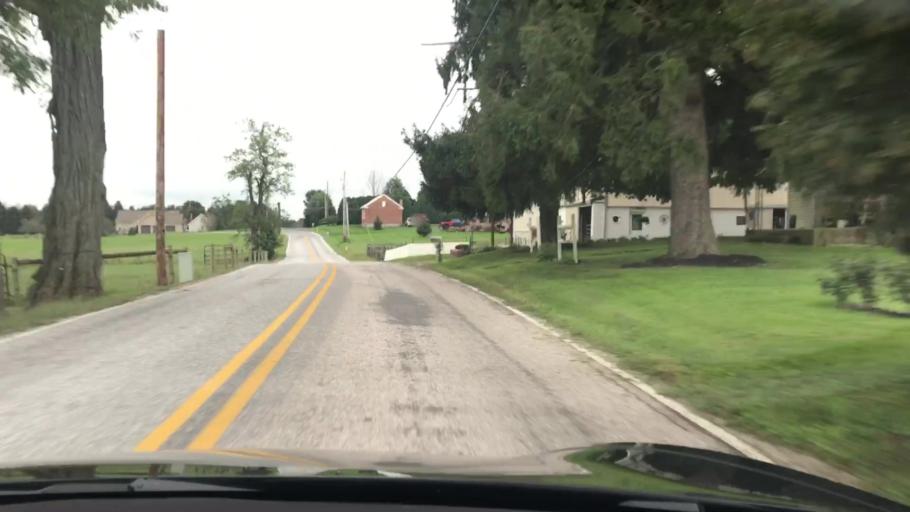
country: US
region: Pennsylvania
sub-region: York County
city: Dillsburg
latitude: 40.0625
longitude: -77.0851
